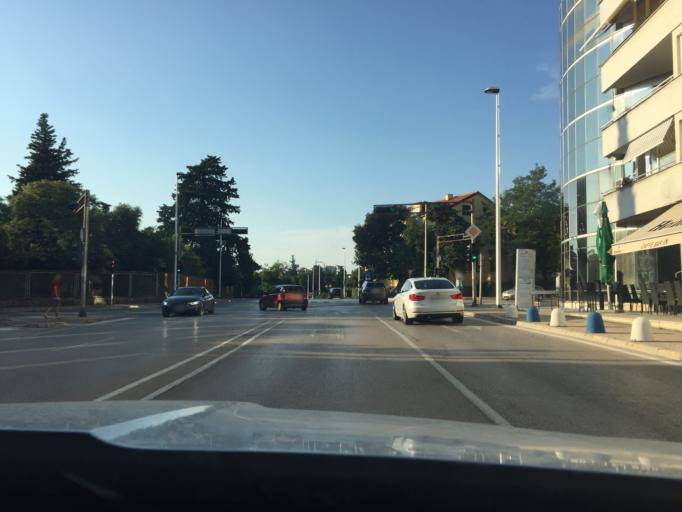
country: HR
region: Zadarska
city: Zadar
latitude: 44.1181
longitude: 15.2353
